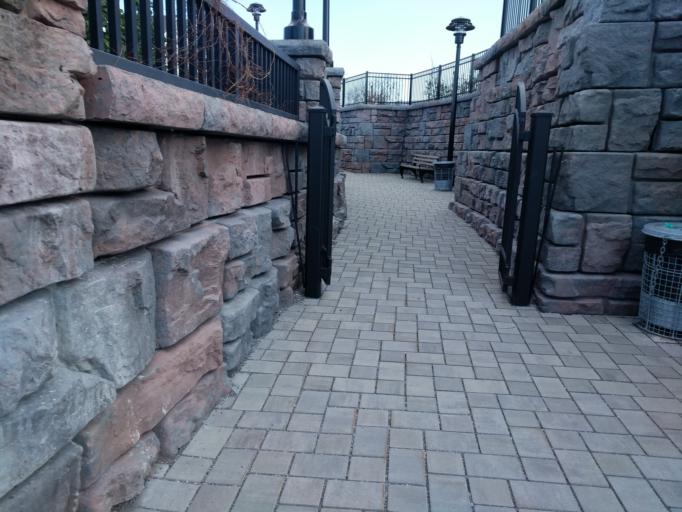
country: US
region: New York
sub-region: Westchester County
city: Pelham Manor
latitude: 40.8481
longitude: -73.7828
